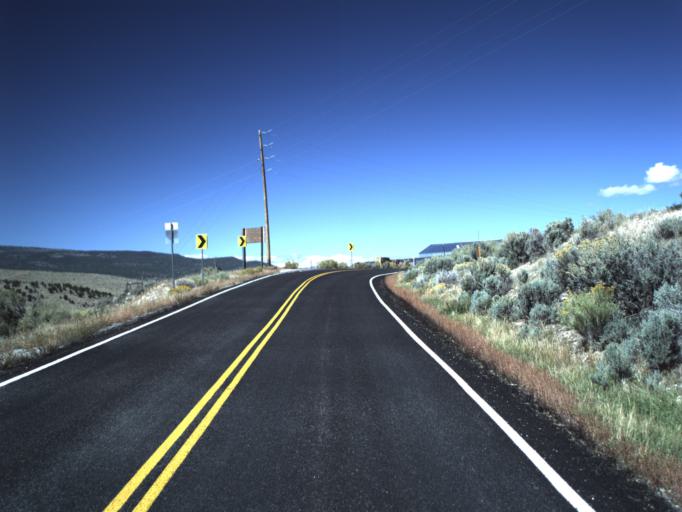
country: US
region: Utah
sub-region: Piute County
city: Junction
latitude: 38.0916
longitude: -111.9824
